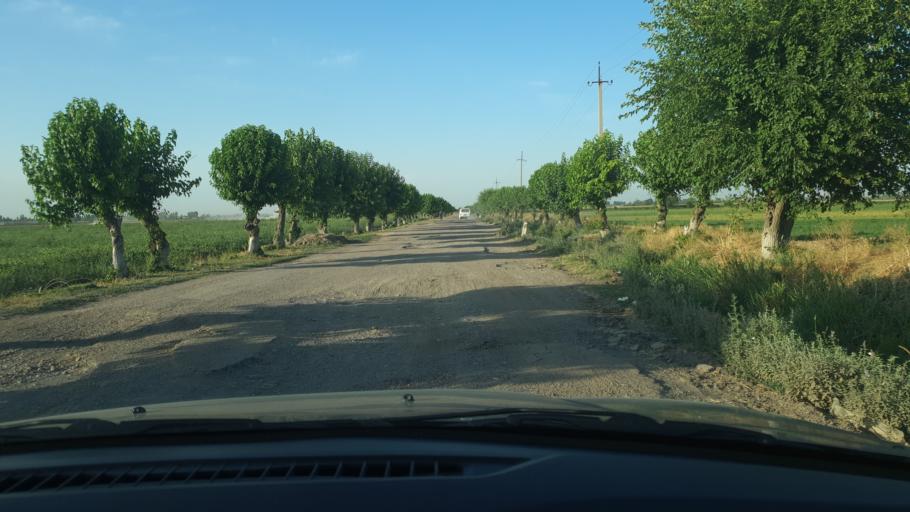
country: UZ
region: Toshkent
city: Tuytepa
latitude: 41.0931
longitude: 69.3705
